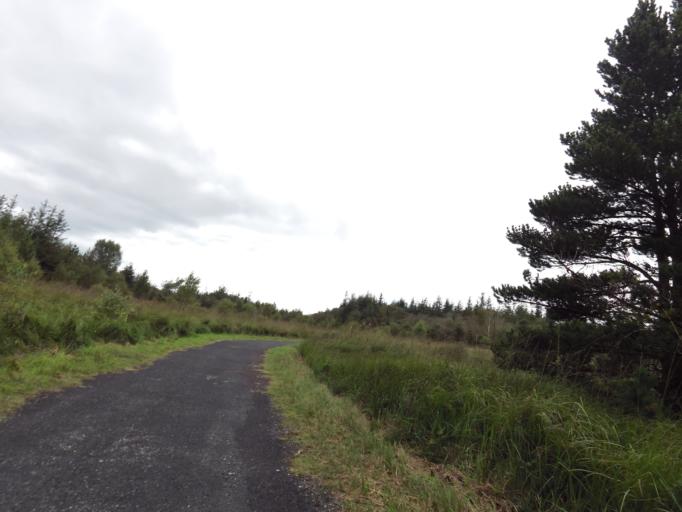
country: IE
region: Leinster
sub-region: Uibh Fhaili
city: Ferbane
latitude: 53.2187
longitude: -7.7524
